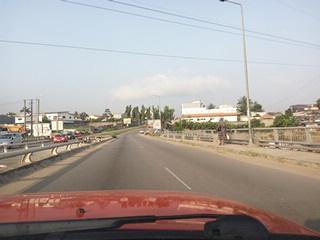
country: CI
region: Lagunes
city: Abobo
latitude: 5.3913
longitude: -3.9826
